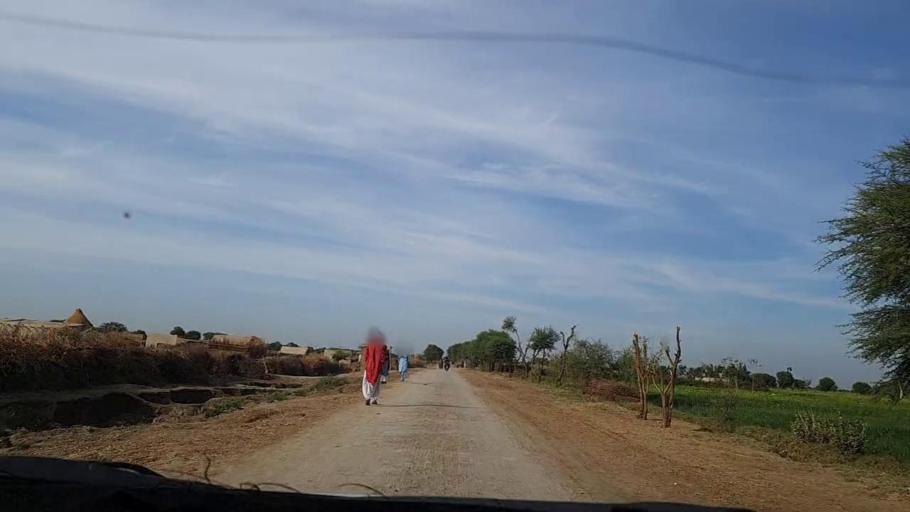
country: PK
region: Sindh
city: Dhoro Naro
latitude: 25.4410
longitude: 69.5122
